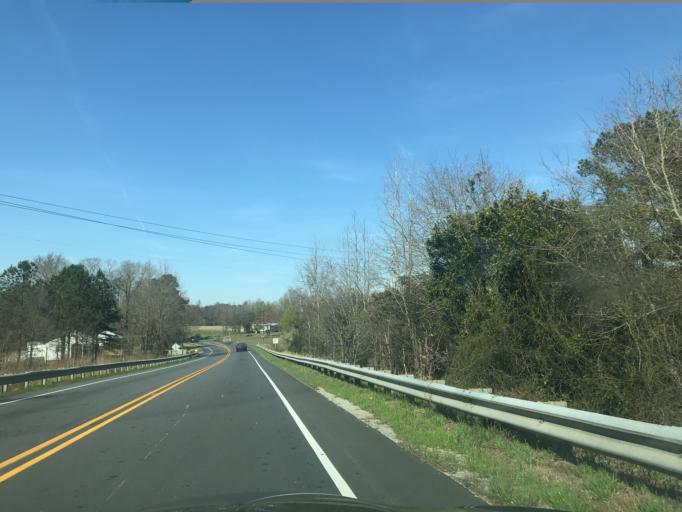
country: US
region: North Carolina
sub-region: Harnett County
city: Angier
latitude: 35.5559
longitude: -78.7553
